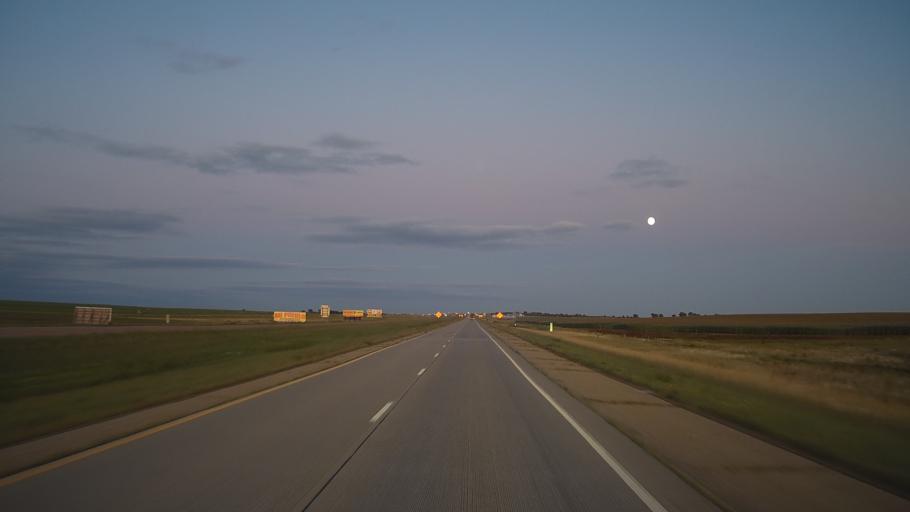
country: US
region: South Dakota
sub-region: Buffalo County
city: Fort Thompson
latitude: 43.8569
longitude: -99.5853
